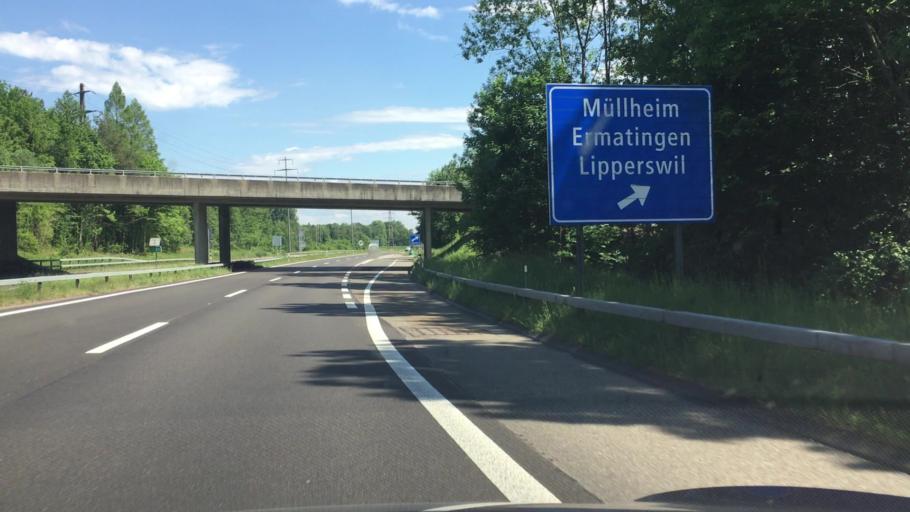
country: CH
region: Thurgau
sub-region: Frauenfeld District
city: Mullheim
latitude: 47.5893
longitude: 9.0000
